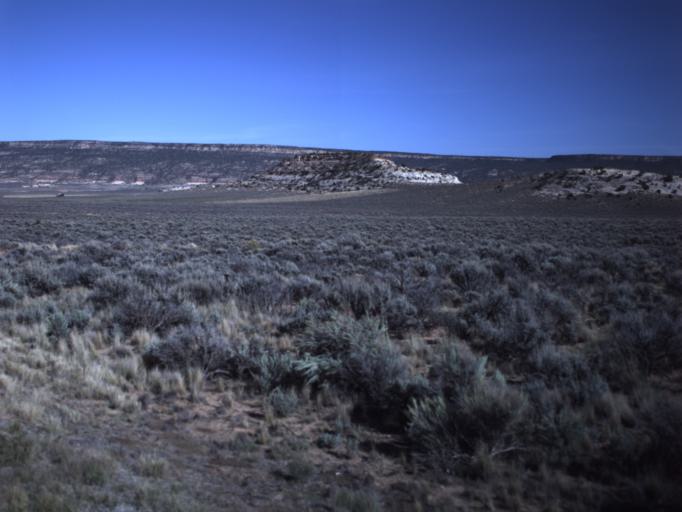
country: US
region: Utah
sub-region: San Juan County
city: Monticello
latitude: 38.0608
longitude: -109.4000
